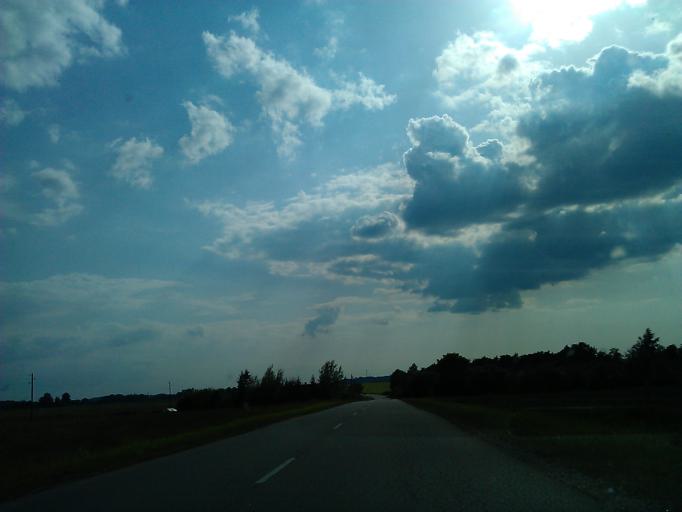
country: LV
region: Aizpute
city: Aizpute
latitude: 56.7287
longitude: 21.6553
